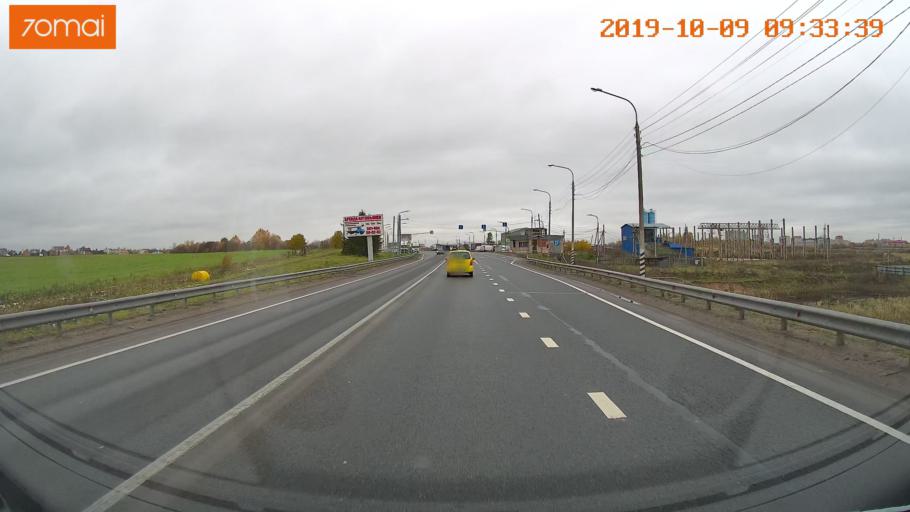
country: RU
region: Vologda
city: Vologda
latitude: 59.1700
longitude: 39.9105
